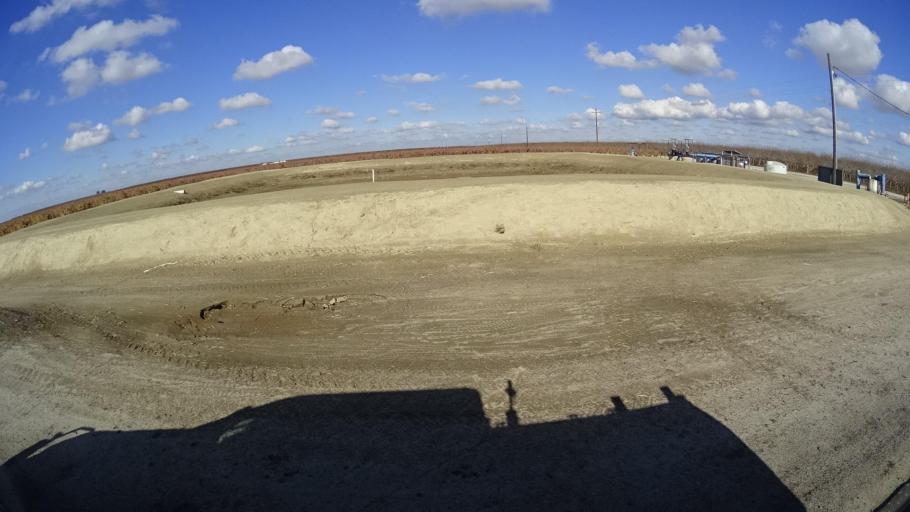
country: US
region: California
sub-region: Kern County
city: Delano
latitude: 35.7322
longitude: -119.3212
